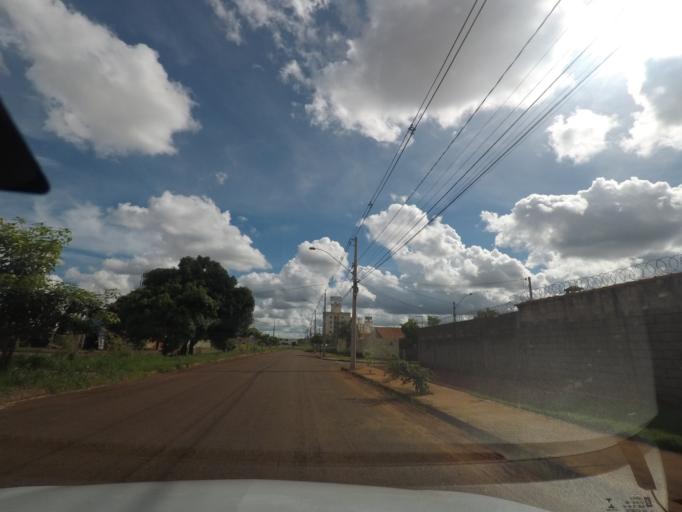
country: BR
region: Goias
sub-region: Goiania
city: Goiania
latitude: -16.7183
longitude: -49.3468
